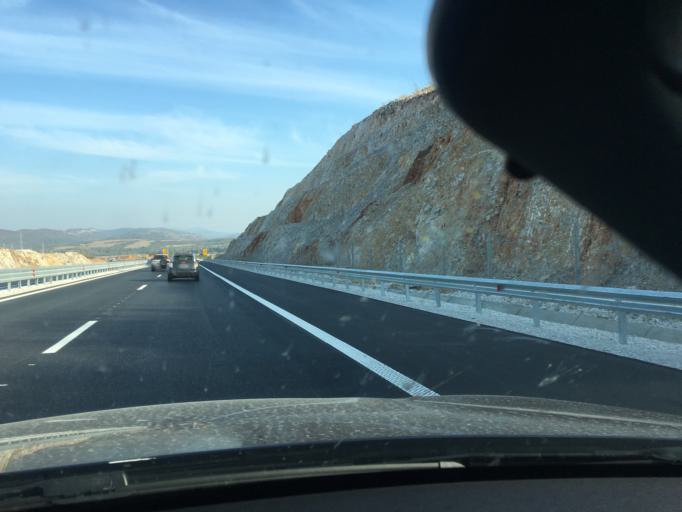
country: BG
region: Lovech
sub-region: Obshtina Yablanitsa
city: Yablanitsa
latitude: 43.0530
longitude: 24.2076
